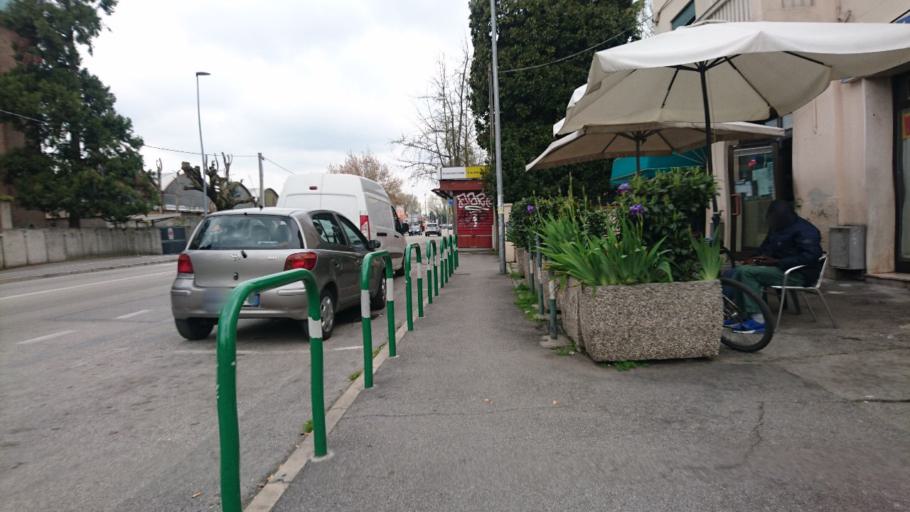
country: IT
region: Veneto
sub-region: Provincia di Padova
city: Padova
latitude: 45.4231
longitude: 11.8739
